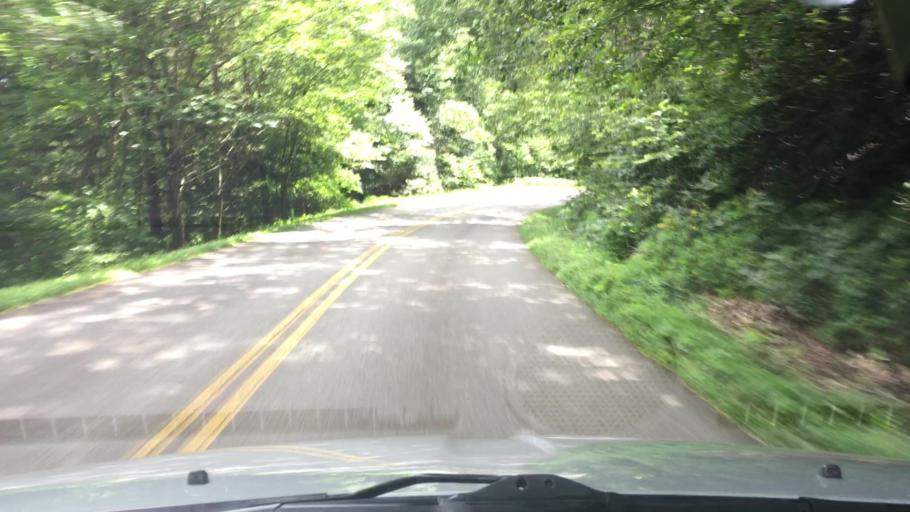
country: US
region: North Carolina
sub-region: Buncombe County
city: Black Mountain
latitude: 35.7050
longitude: -82.2639
